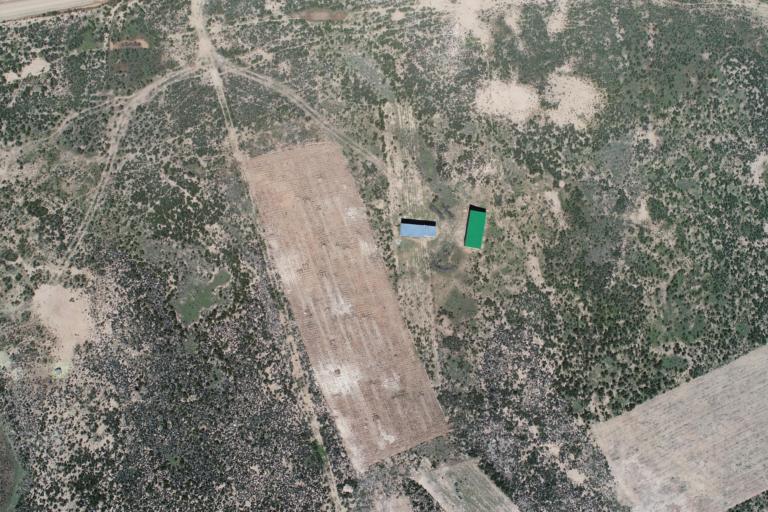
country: BO
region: La Paz
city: Patacamaya
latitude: -17.2929
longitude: -68.4874
